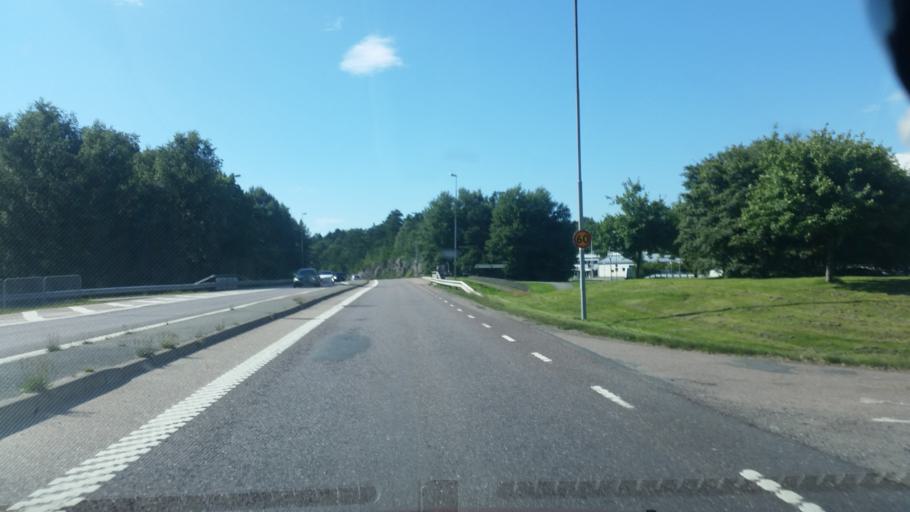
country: SE
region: Vaestra Goetaland
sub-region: Partille Kommun
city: Furulund
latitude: 57.7242
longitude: 12.1285
